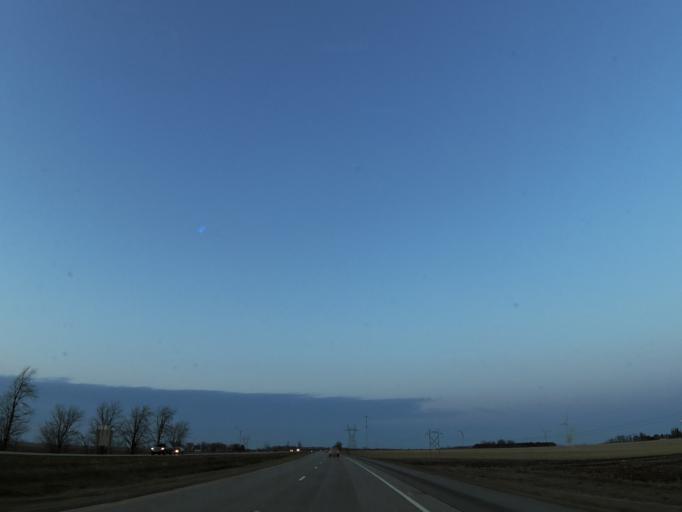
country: US
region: Minnesota
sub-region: Mower County
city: Grand Meadow
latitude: 43.7237
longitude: -92.6827
